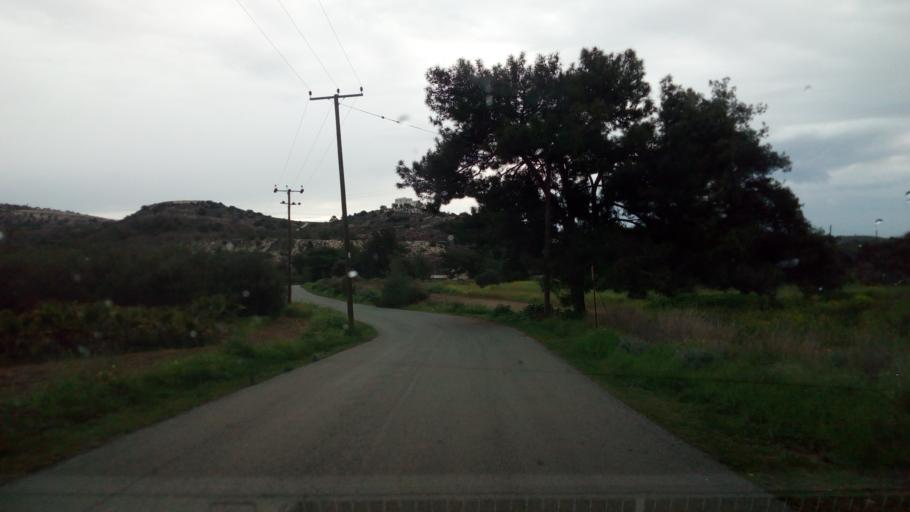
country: CY
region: Larnaka
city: Kofinou
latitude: 34.8583
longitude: 33.4503
